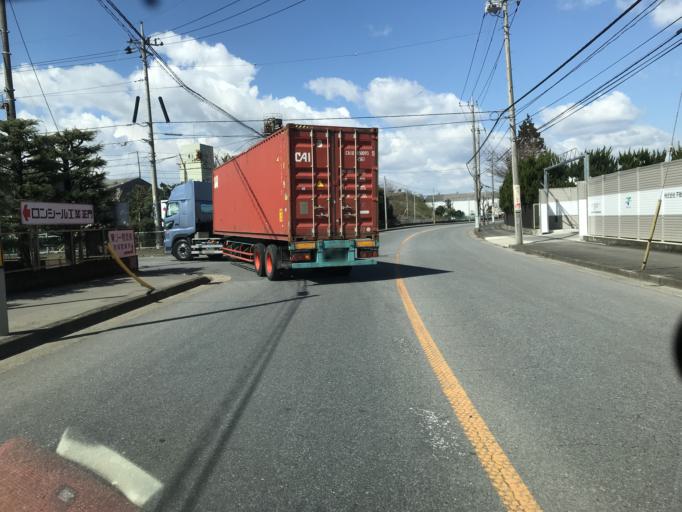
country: JP
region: Ibaraki
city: Ishioka
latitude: 36.1214
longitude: 140.2173
